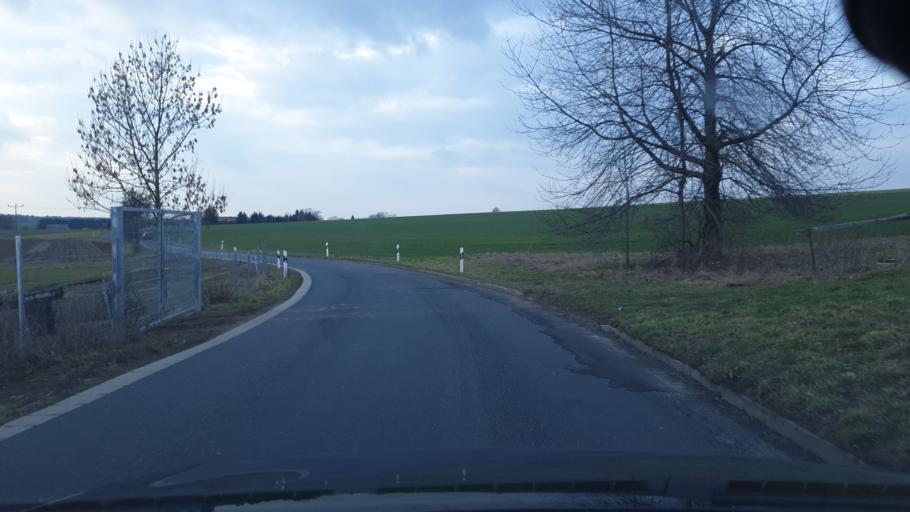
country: DE
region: Saxony
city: Erlau
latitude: 50.9902
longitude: 12.9241
